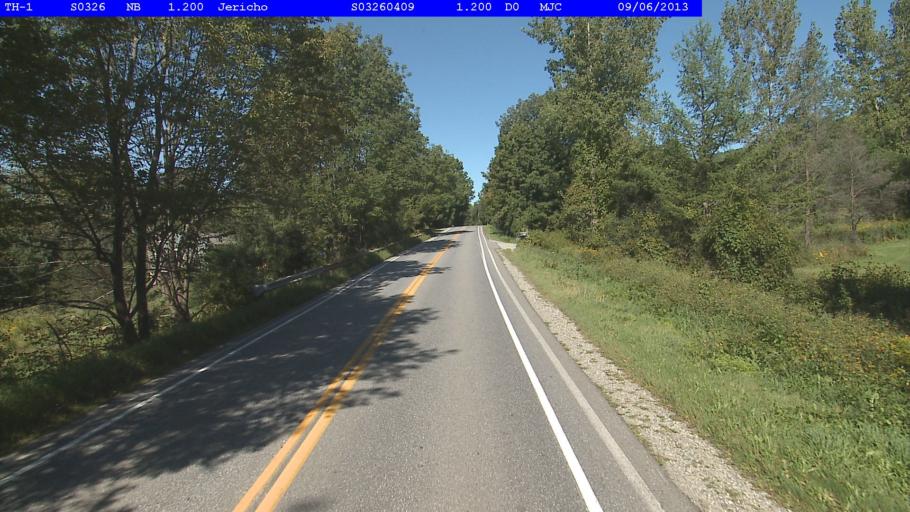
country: US
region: Vermont
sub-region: Chittenden County
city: Jericho
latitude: 44.4948
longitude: -72.9572
